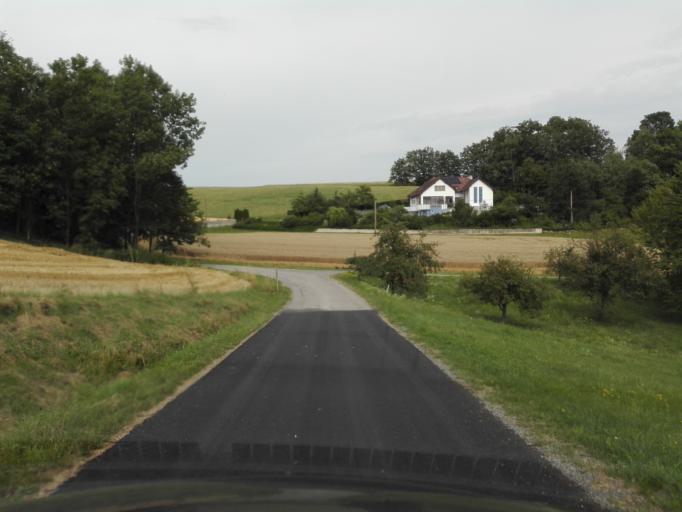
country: AT
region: Upper Austria
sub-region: Politischer Bezirk Perg
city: Perg
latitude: 48.2291
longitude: 14.7158
